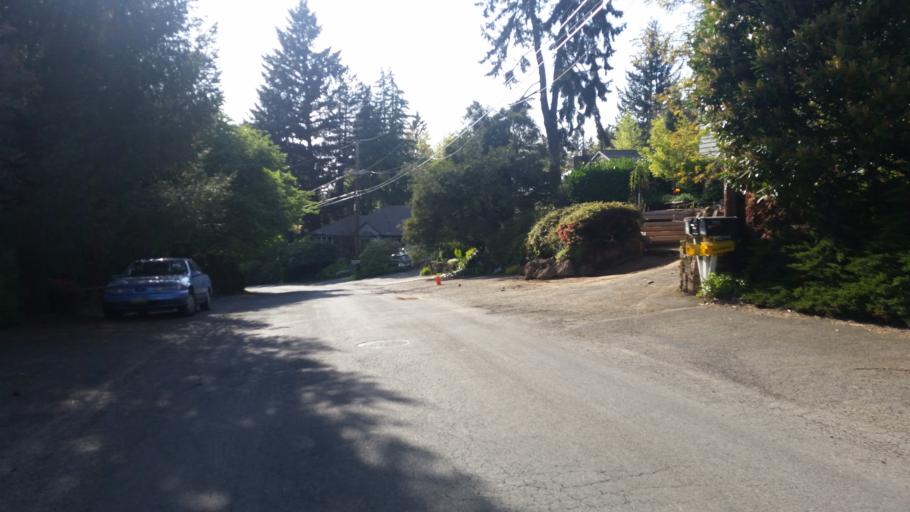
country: US
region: Oregon
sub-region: Multnomah County
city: Portland
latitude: 45.4811
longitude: -122.6943
